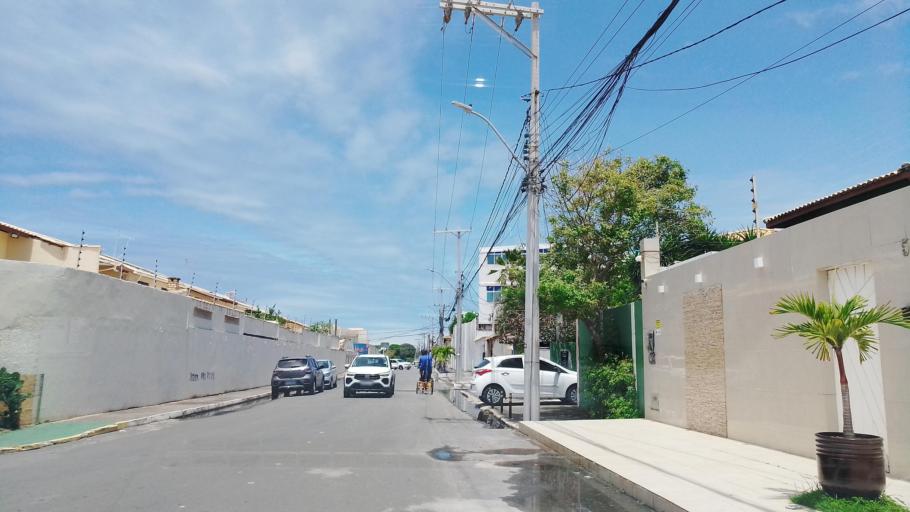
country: BR
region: Bahia
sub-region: Lauro De Freitas
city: Lauro de Freitas
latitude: -12.9362
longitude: -38.3299
